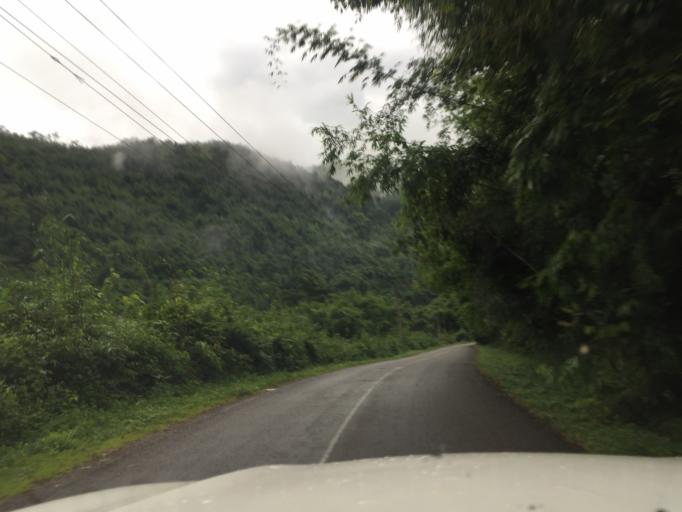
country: LA
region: Oudomxai
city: Muang La
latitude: 20.9011
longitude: 102.1811
